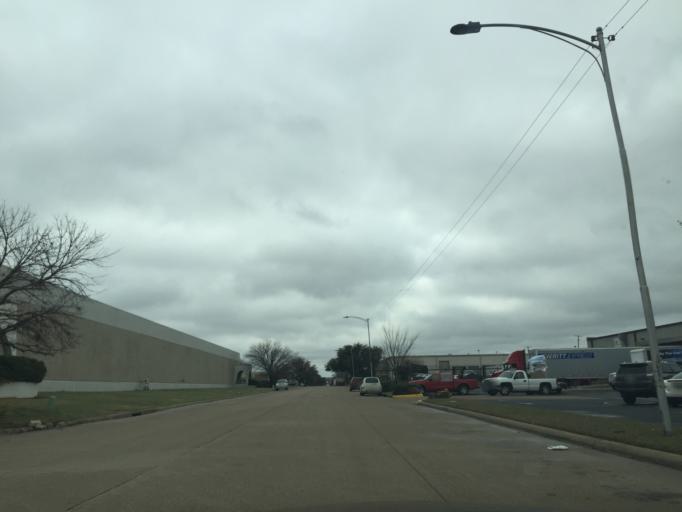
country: US
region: Texas
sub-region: Dallas County
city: Grand Prairie
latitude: 32.7550
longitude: -97.0492
